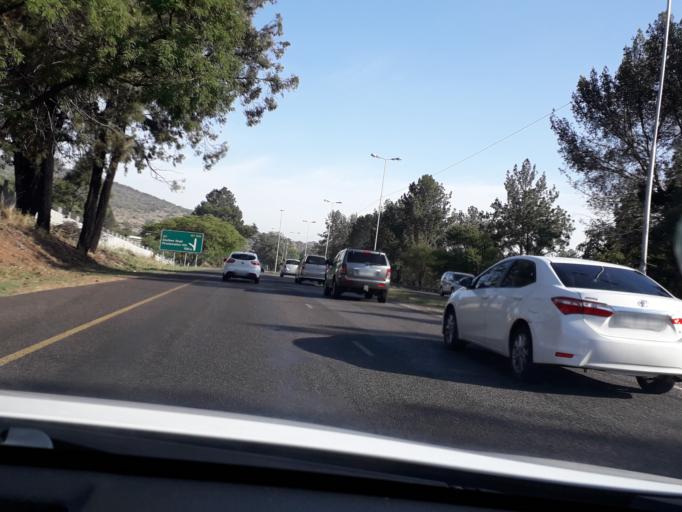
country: ZA
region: Gauteng
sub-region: City of Tshwane Metropolitan Municipality
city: Pretoria
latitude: -25.7880
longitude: 28.1951
